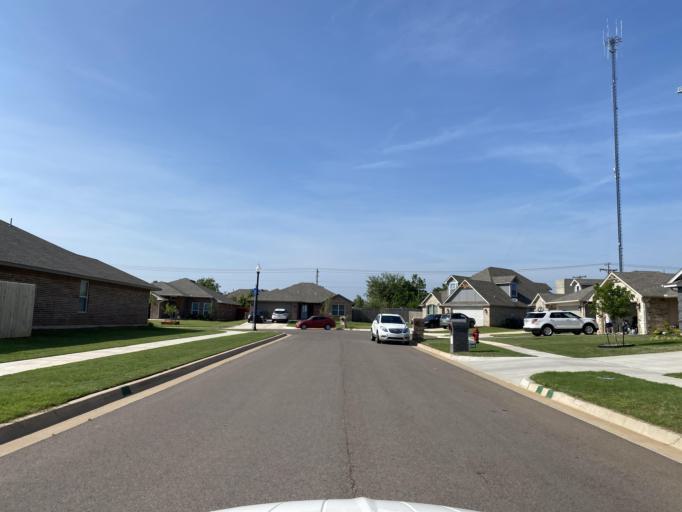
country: US
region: Oklahoma
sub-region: Oklahoma County
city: Nicoma Park
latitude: 35.4417
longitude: -97.3417
